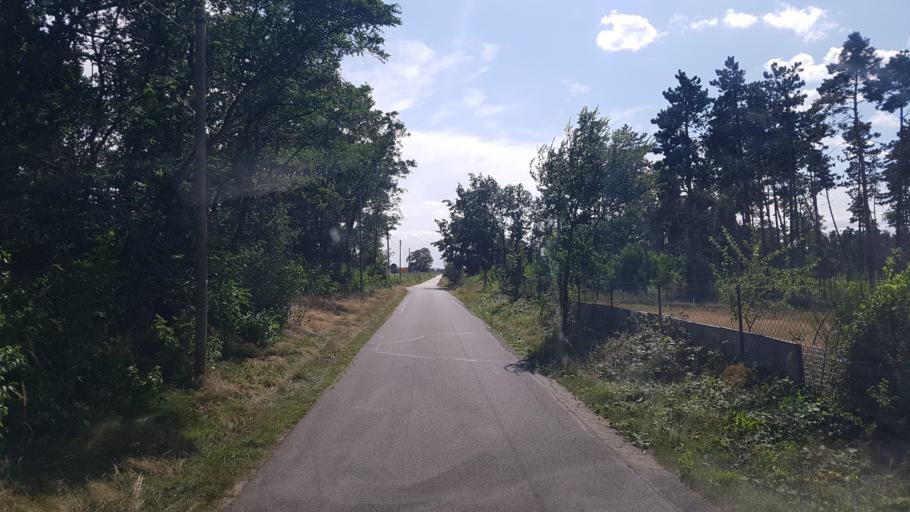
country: DE
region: Brandenburg
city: Muhlberg
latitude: 51.4454
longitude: 13.2914
